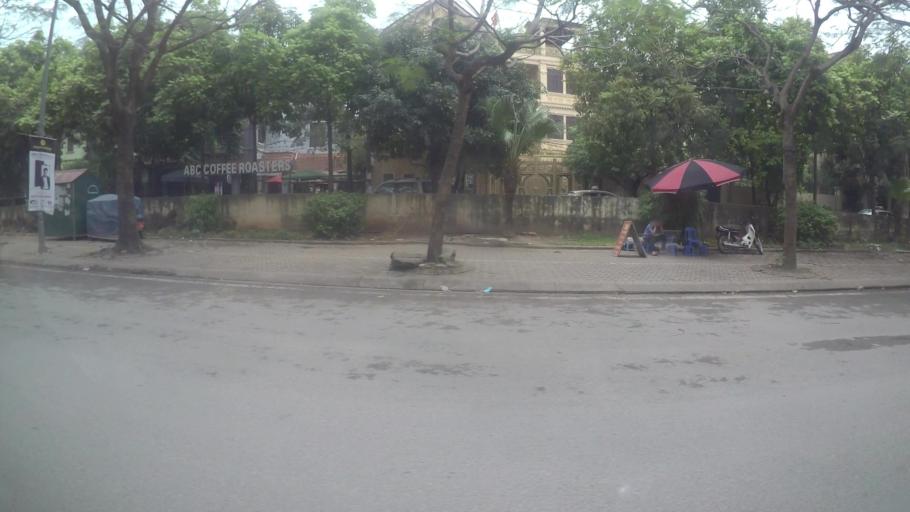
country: VN
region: Ha Noi
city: Tay Ho
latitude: 21.0680
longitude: 105.8034
